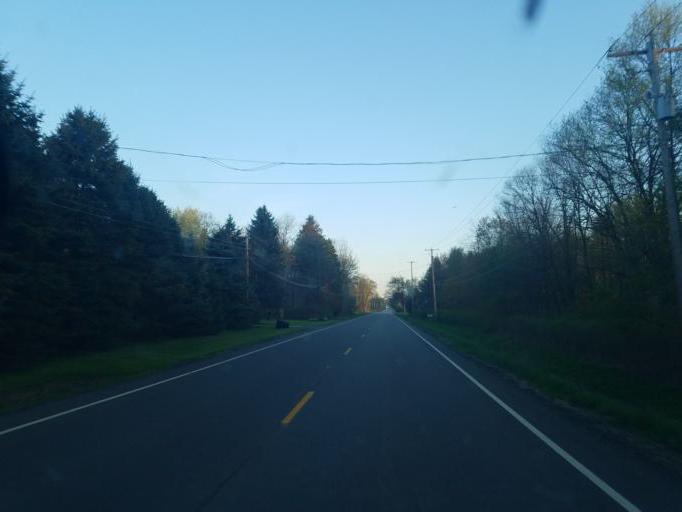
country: US
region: Ohio
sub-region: Trumbull County
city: Brookfield Center
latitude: 41.3265
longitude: -80.5683
